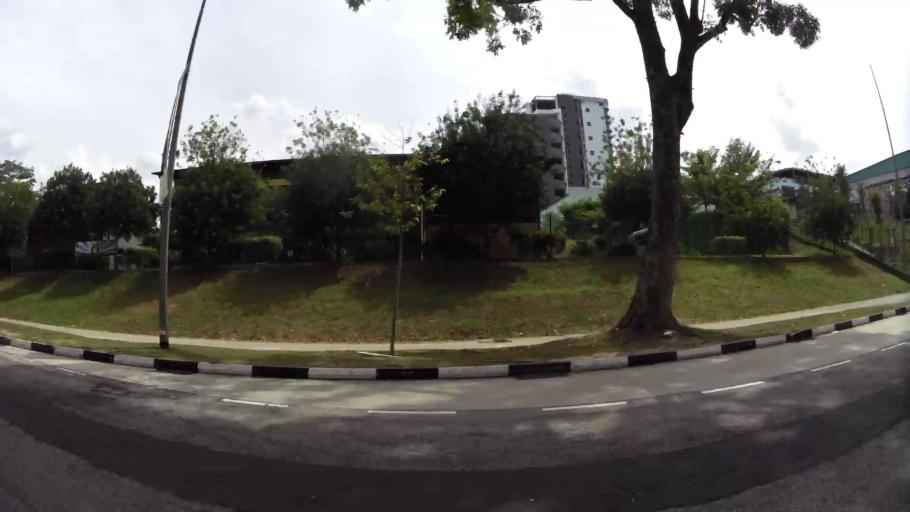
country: MY
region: Johor
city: Johor Bahru
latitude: 1.4117
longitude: 103.7583
